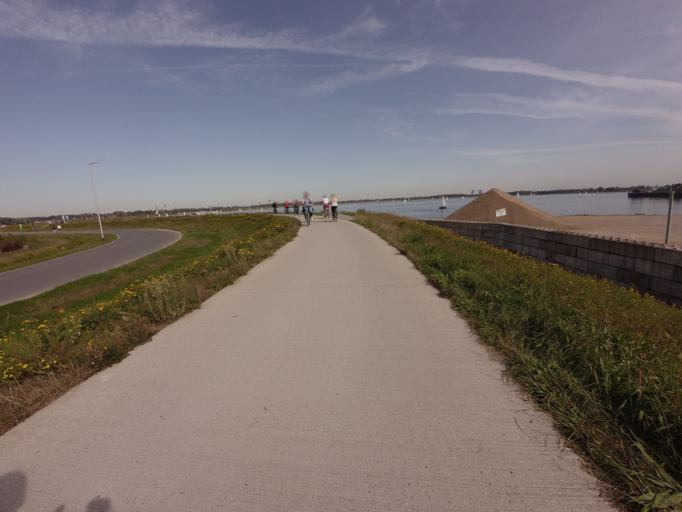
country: BE
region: Flanders
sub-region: Provincie Limburg
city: Maaseik
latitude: 51.1365
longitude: 5.8202
